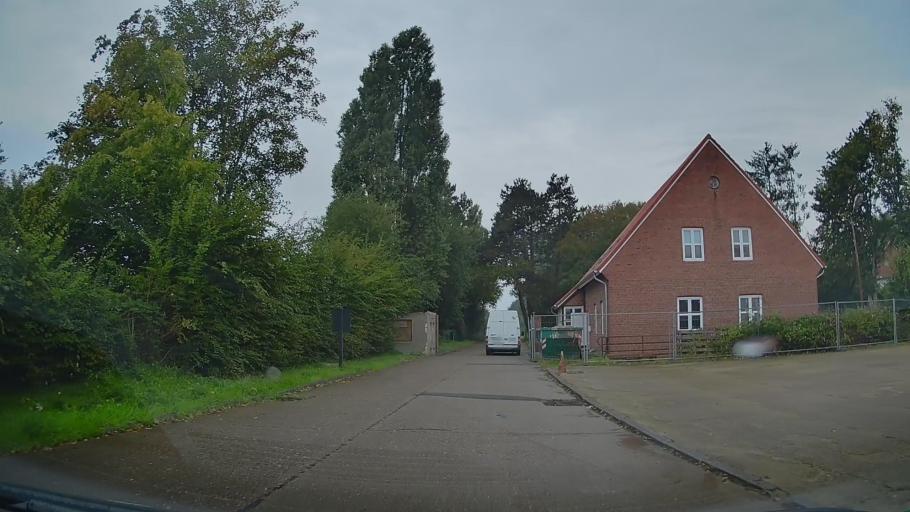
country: DE
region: Mecklenburg-Vorpommern
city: Dassow
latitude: 53.9155
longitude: 10.9721
